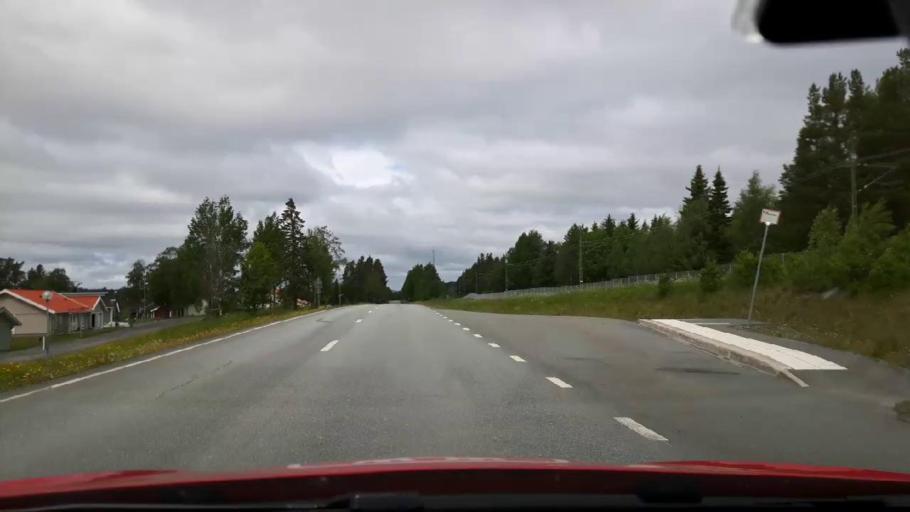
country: SE
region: Jaemtland
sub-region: Krokoms Kommun
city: Krokom
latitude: 63.2916
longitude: 14.4930
